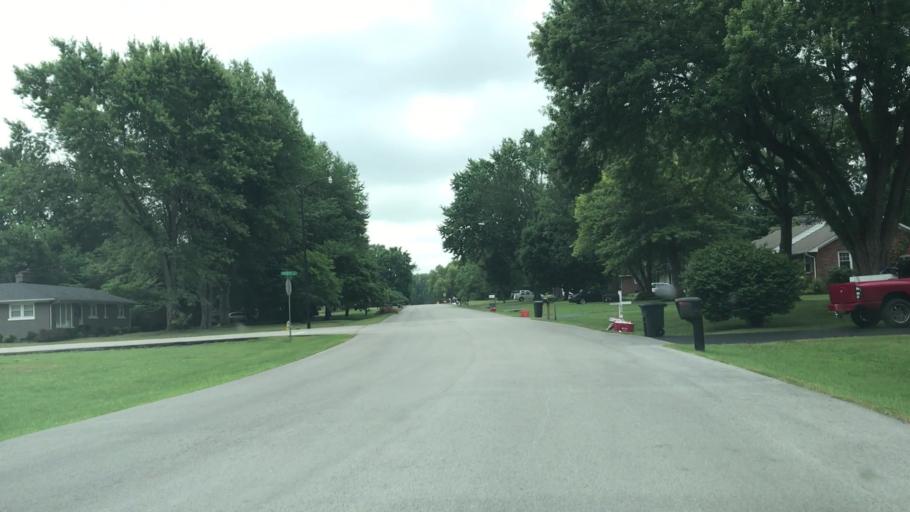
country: US
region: Kentucky
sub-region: Warren County
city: Bowling Green
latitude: 36.9890
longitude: -86.4159
